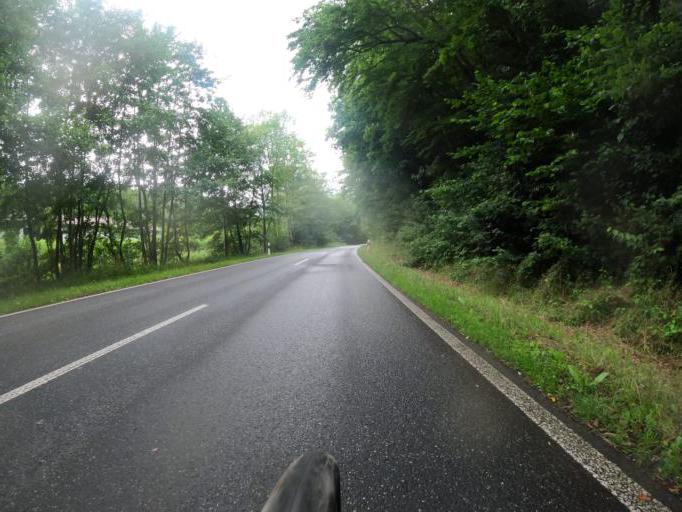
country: DE
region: Thuringia
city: Lindewerra
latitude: 51.3042
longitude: 9.9219
